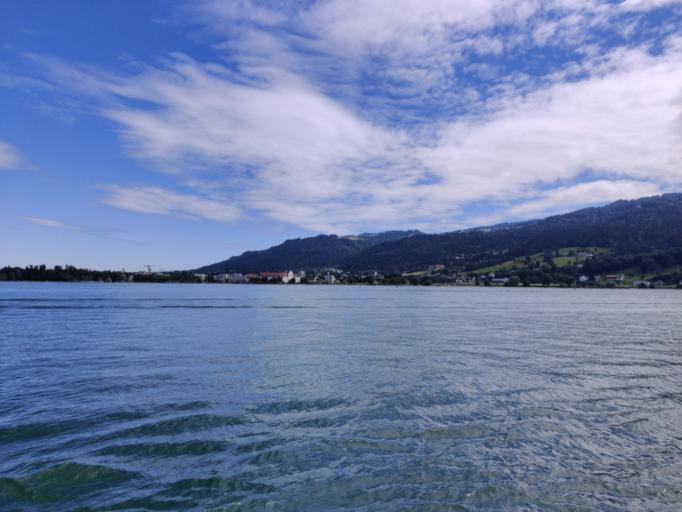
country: AT
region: Vorarlberg
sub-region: Politischer Bezirk Bregenz
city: Bregenz
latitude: 47.5191
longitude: 9.7355
